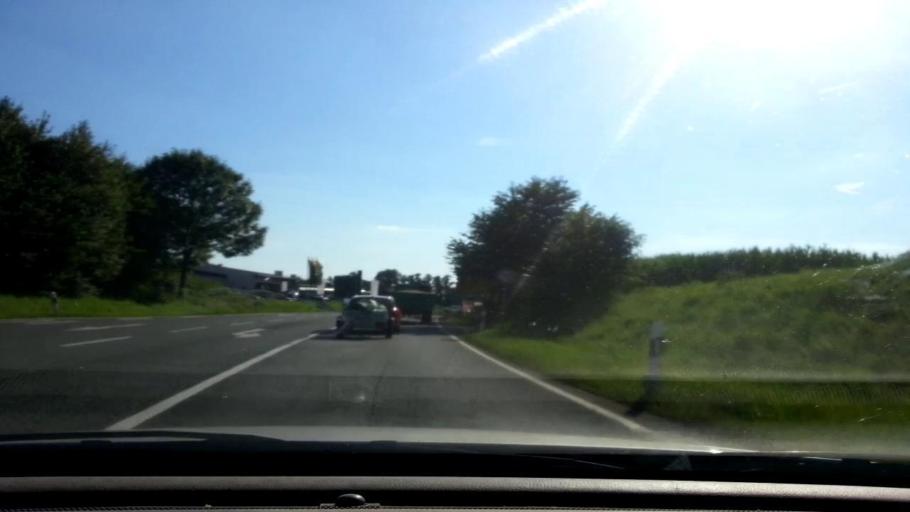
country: DE
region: Bavaria
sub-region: Upper Franconia
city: Schesslitz
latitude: 49.9815
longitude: 11.0442
